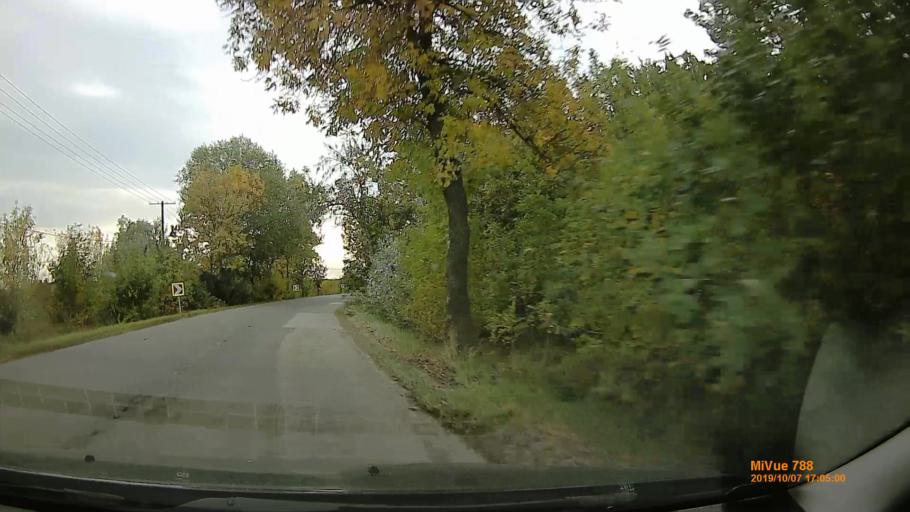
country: HU
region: Bekes
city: Szarvas
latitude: 46.8284
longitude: 20.5419
